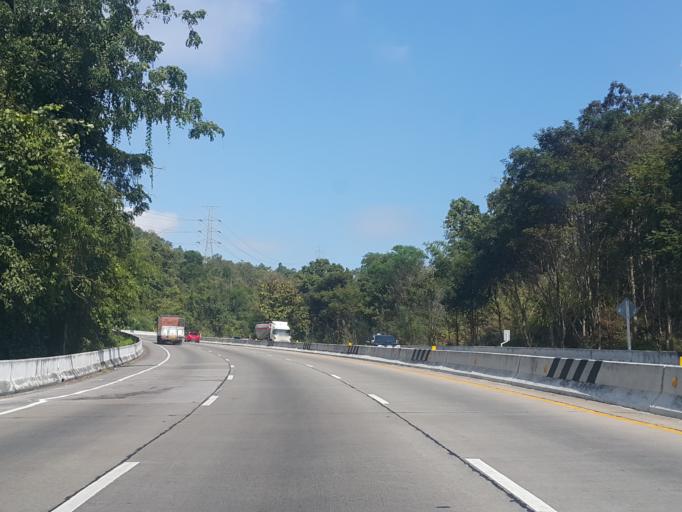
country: TH
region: Lamphun
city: Mae Tha
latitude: 18.4149
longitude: 99.2094
